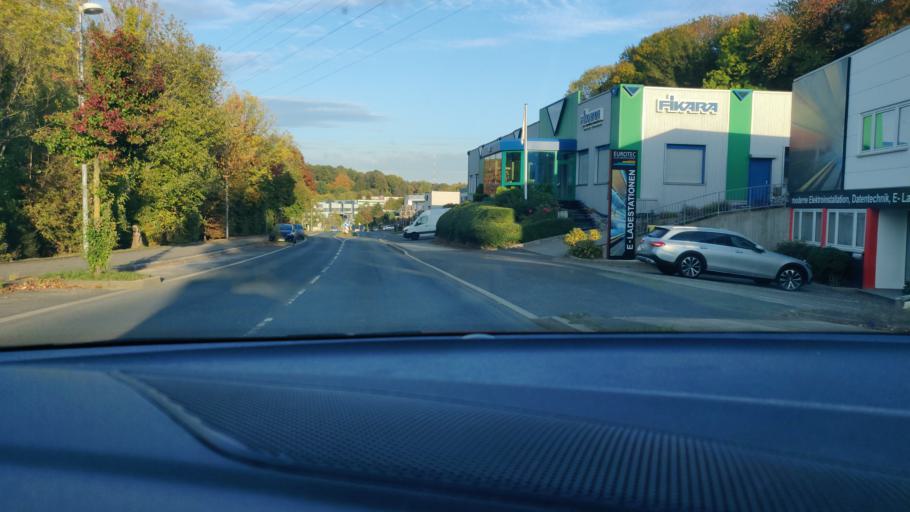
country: DE
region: North Rhine-Westphalia
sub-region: Regierungsbezirk Dusseldorf
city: Velbert
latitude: 51.3499
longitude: 7.0724
